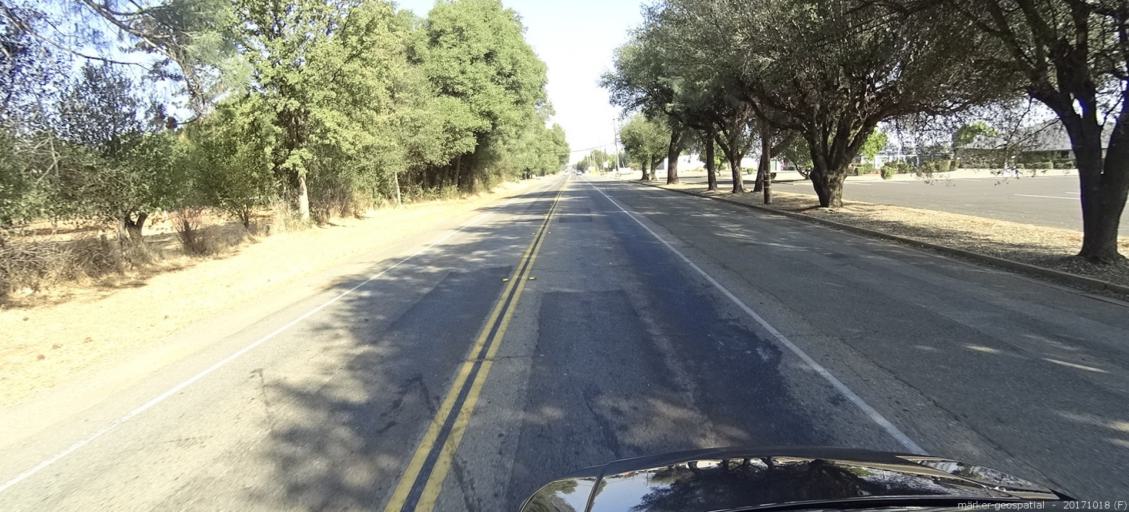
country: US
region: California
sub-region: Shasta County
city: Palo Cedro
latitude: 40.5377
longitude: -122.3028
